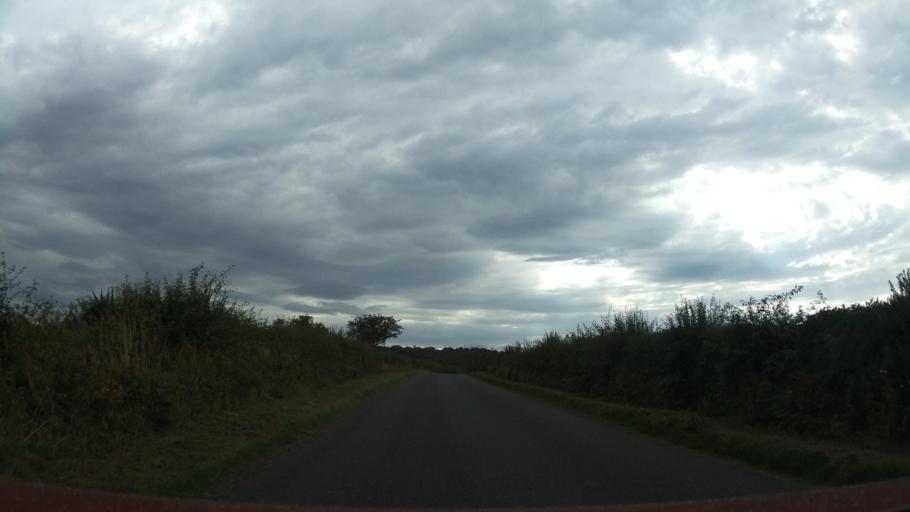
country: GB
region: Scotland
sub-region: Fife
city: Saint Andrews
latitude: 56.3025
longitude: -2.7868
